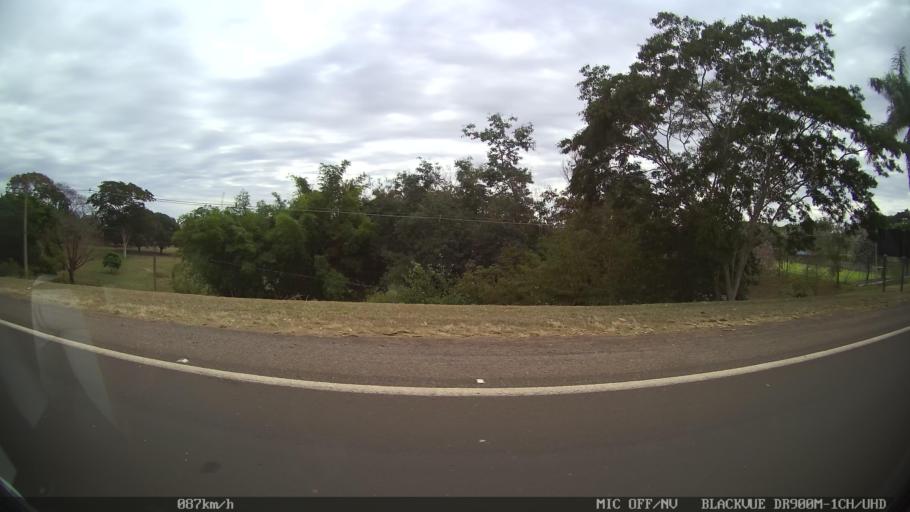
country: BR
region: Sao Paulo
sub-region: Sao Jose Do Rio Preto
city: Sao Jose do Rio Preto
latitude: -20.8160
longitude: -49.4455
